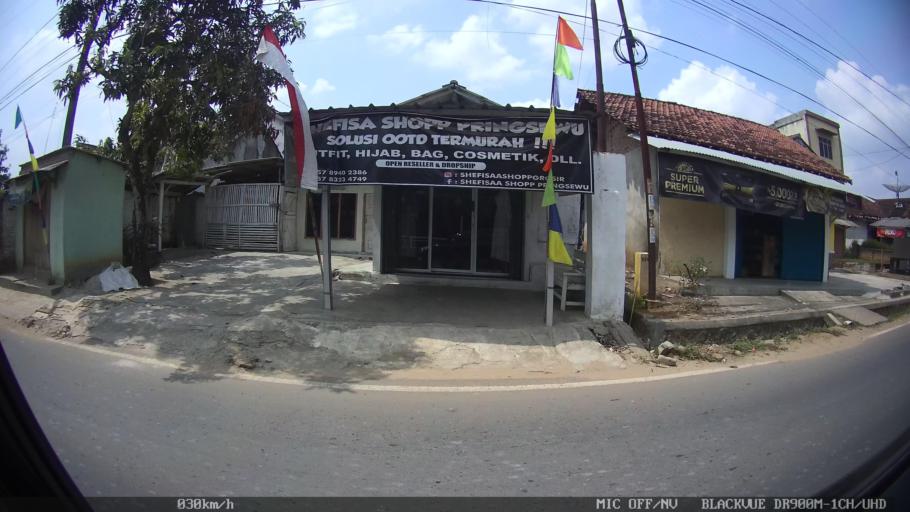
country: ID
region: Lampung
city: Pringsewu
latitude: -5.3671
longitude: 104.9692
